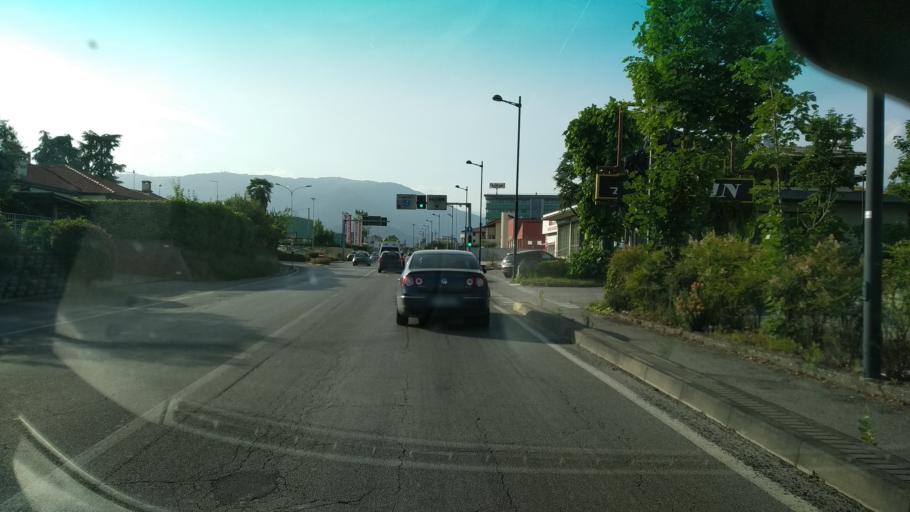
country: IT
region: Veneto
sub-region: Provincia di Vicenza
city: San Zeno-San Giuseppe
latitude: 45.7488
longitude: 11.7500
